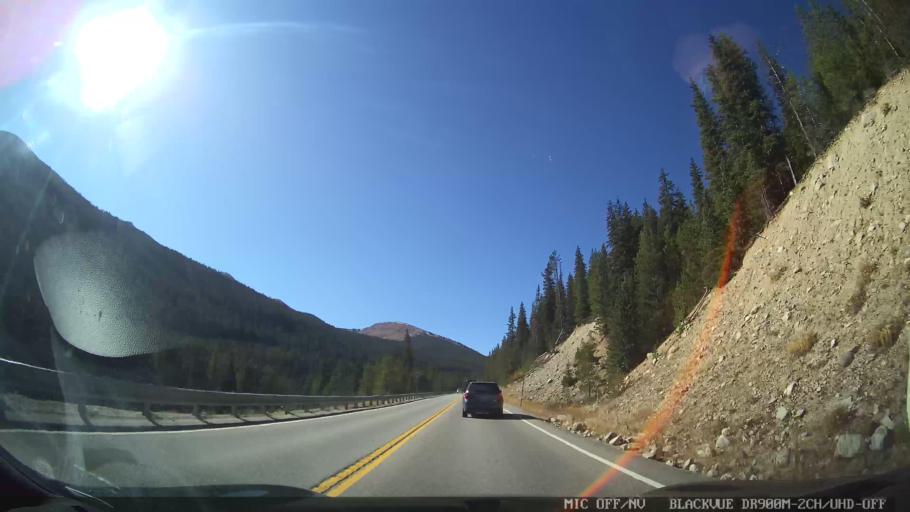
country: US
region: Colorado
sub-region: Summit County
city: Breckenridge
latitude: 39.4726
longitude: -106.1314
